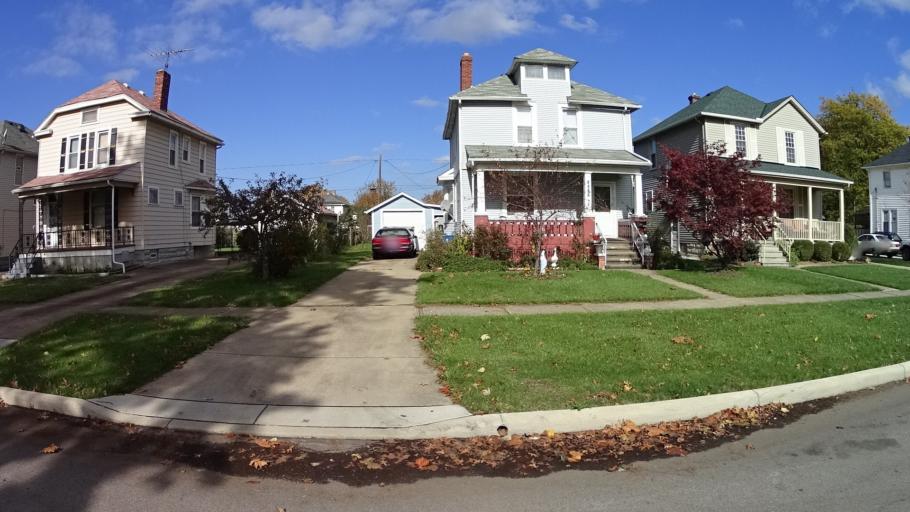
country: US
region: Ohio
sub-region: Lorain County
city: Sheffield
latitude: 41.4437
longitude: -82.1161
